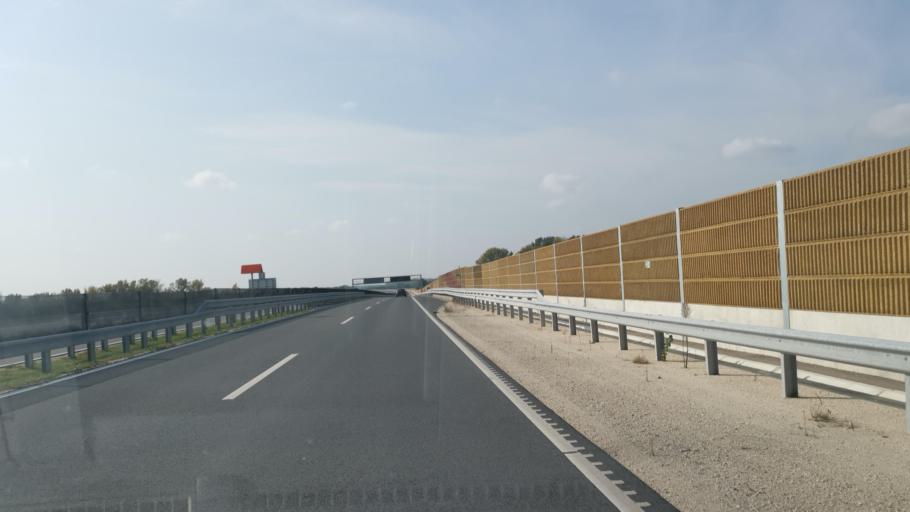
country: HU
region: Gyor-Moson-Sopron
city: Farad
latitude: 47.5846
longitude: 17.1764
